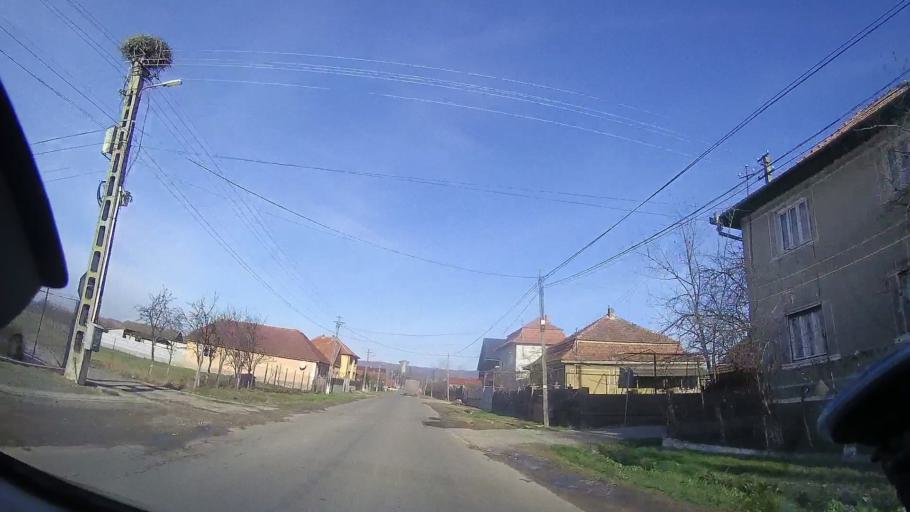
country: RO
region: Bihor
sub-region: Comuna Astileu
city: Astileu
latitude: 47.0339
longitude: 22.3901
